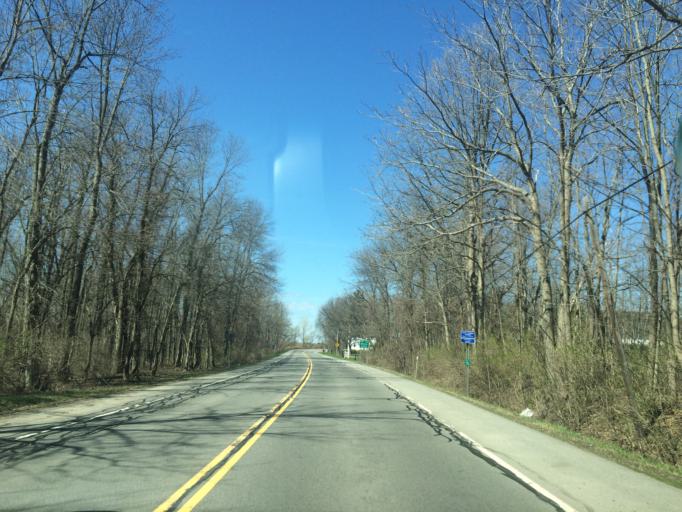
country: US
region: New York
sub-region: Monroe County
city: Fairport
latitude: 43.0956
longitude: -77.3735
